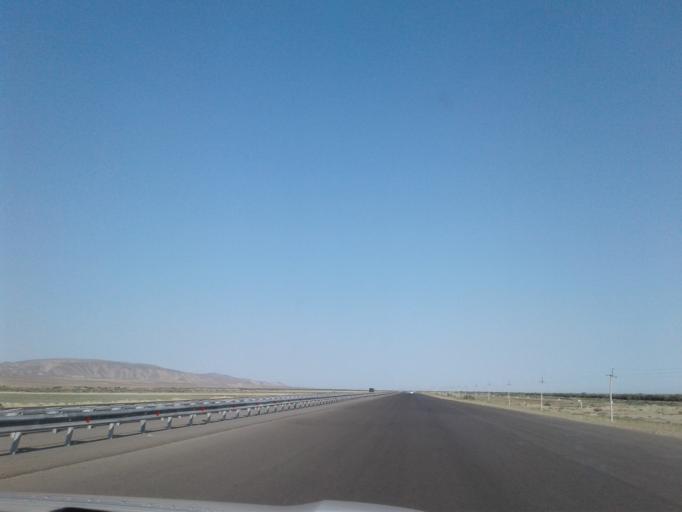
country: TM
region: Balkan
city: Serdar
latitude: 38.8946
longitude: 56.5239
